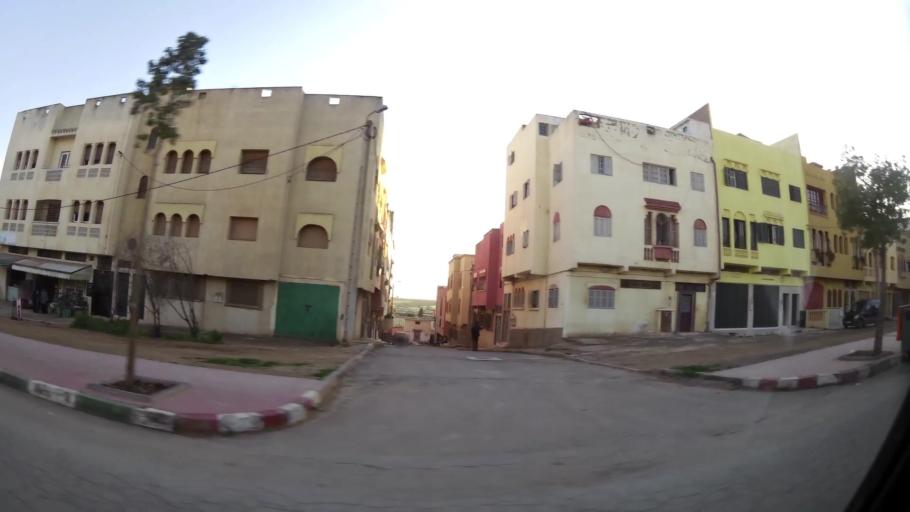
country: MA
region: Chaouia-Ouardigha
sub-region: Settat Province
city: Settat
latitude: 32.9899
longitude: -7.6111
